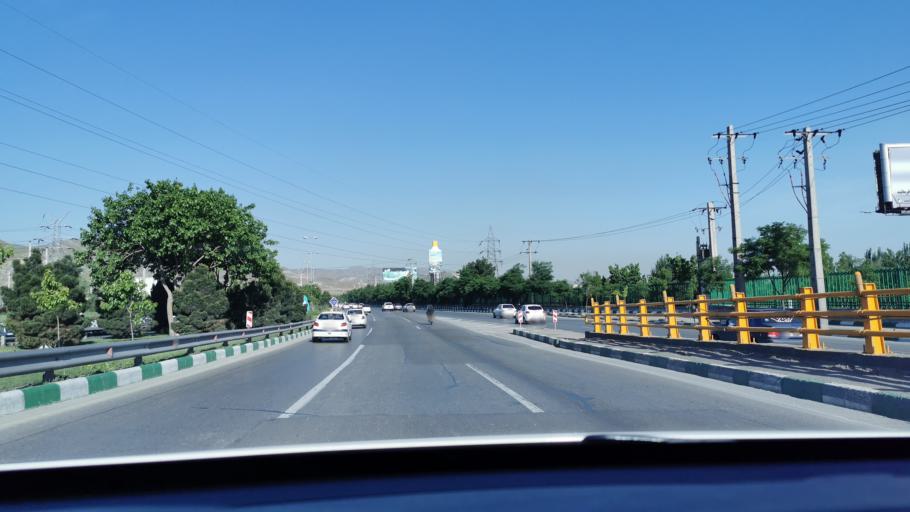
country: IR
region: Razavi Khorasan
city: Mashhad
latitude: 36.2568
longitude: 59.5958
